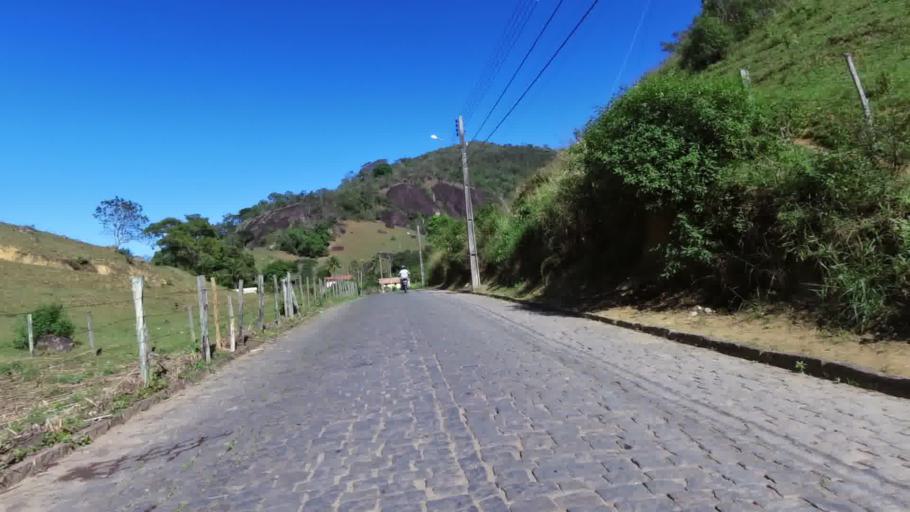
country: BR
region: Espirito Santo
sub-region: Rio Novo Do Sul
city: Rio Novo do Sul
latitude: -20.8554
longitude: -40.9293
